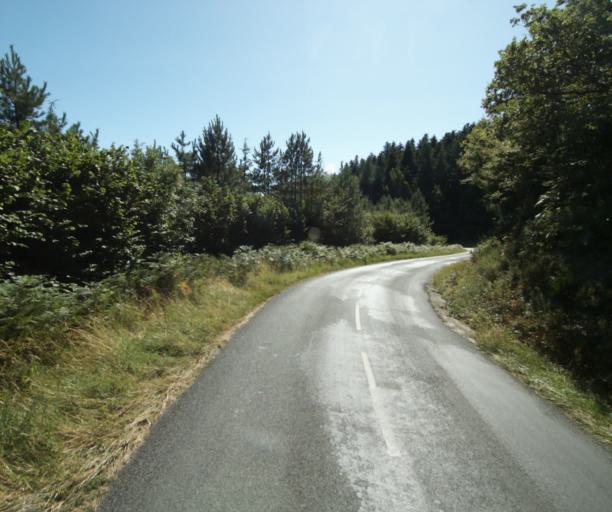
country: FR
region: Midi-Pyrenees
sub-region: Departement du Tarn
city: Dourgne
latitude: 43.4403
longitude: 2.1423
